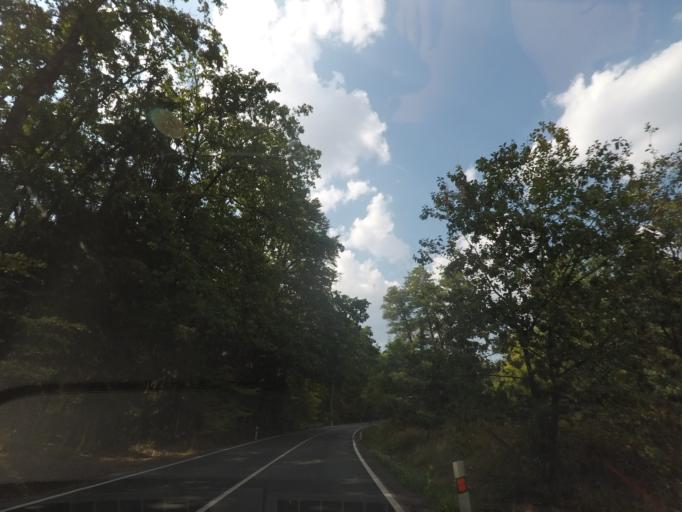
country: CZ
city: Borohradek
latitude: 50.1075
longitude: 16.0784
